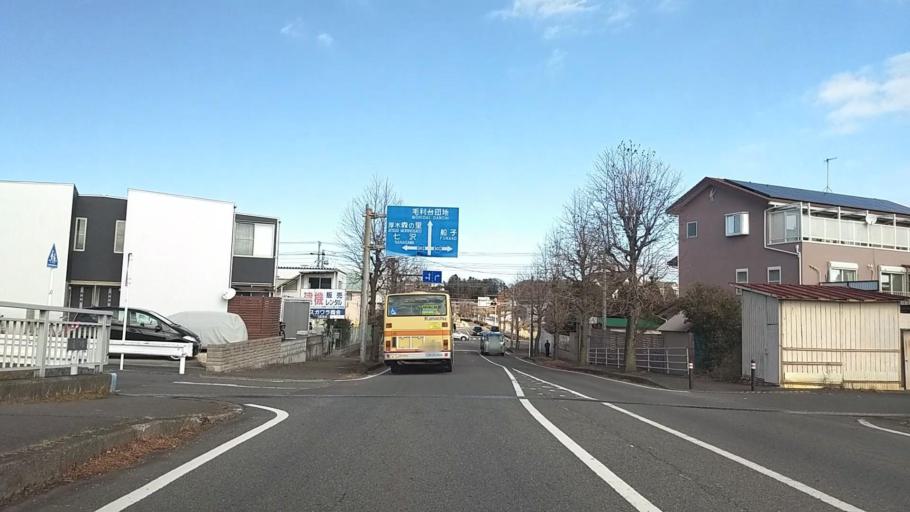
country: JP
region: Kanagawa
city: Atsugi
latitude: 35.4301
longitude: 139.3295
